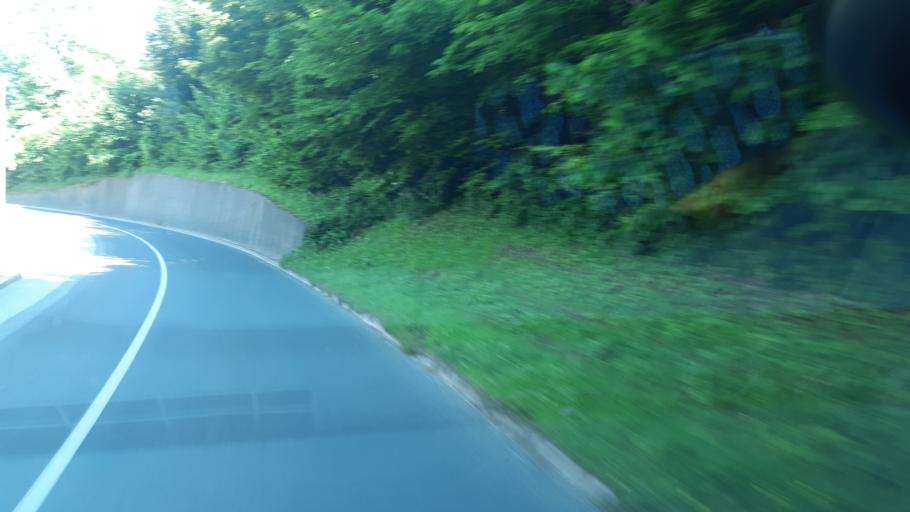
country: SI
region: Kranj
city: Kranj
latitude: 46.2185
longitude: 14.3695
